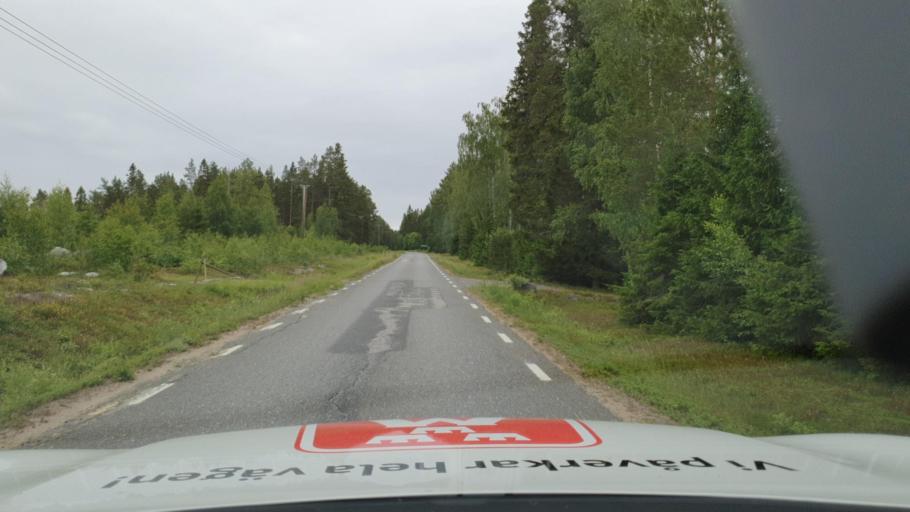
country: SE
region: Vaesterbotten
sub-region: Nordmalings Kommun
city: Nordmaling
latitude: 63.4387
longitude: 19.4693
